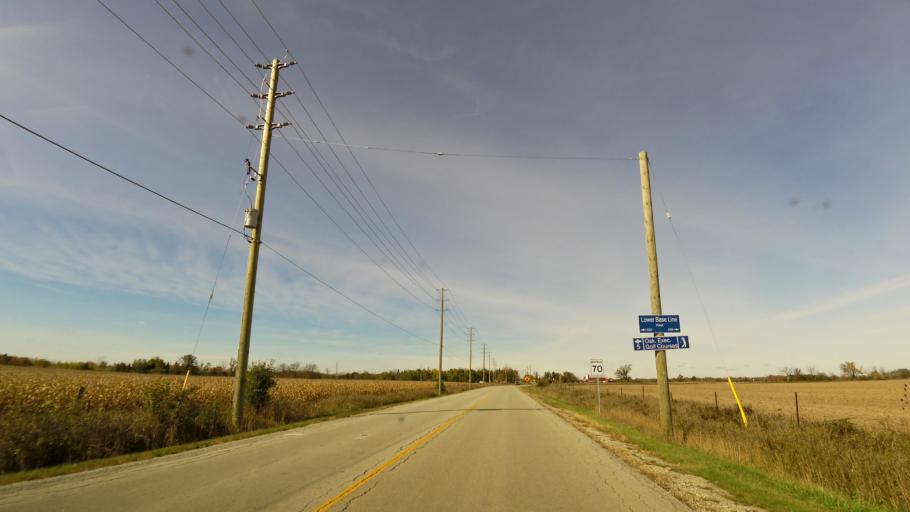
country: CA
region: Ontario
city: Oakville
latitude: 43.5036
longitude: -79.7623
